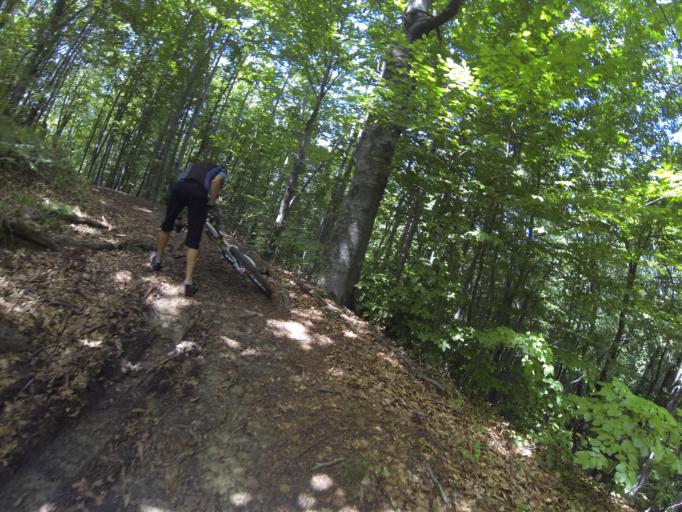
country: RO
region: Valcea
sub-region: Oras Baile Olanesti
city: Baile Olanesti
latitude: 45.2183
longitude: 24.1989
